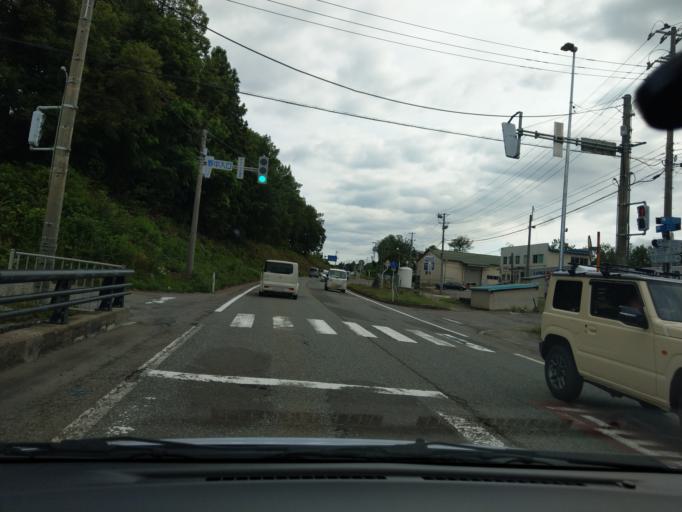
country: JP
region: Akita
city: Yokotemachi
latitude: 39.3427
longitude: 140.5597
